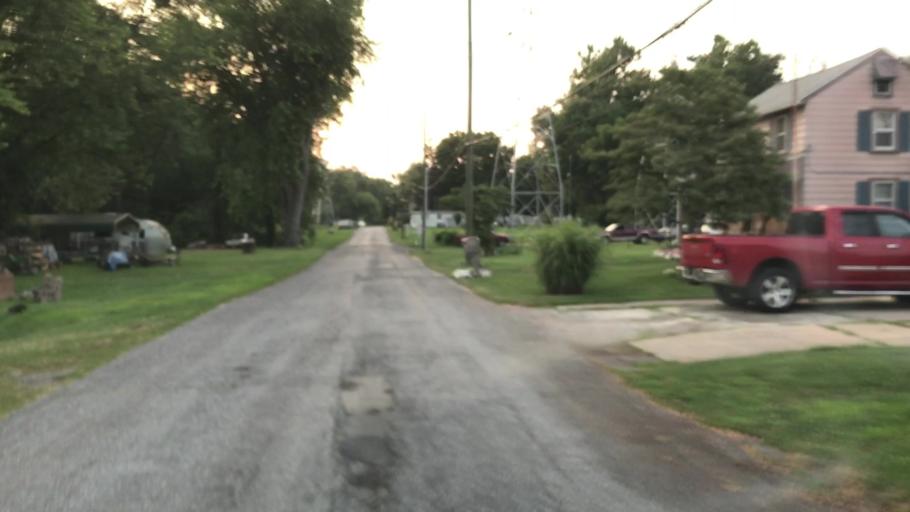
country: US
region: Pennsylvania
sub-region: Dauphin County
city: Middletown
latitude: 40.1835
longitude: -76.7296
